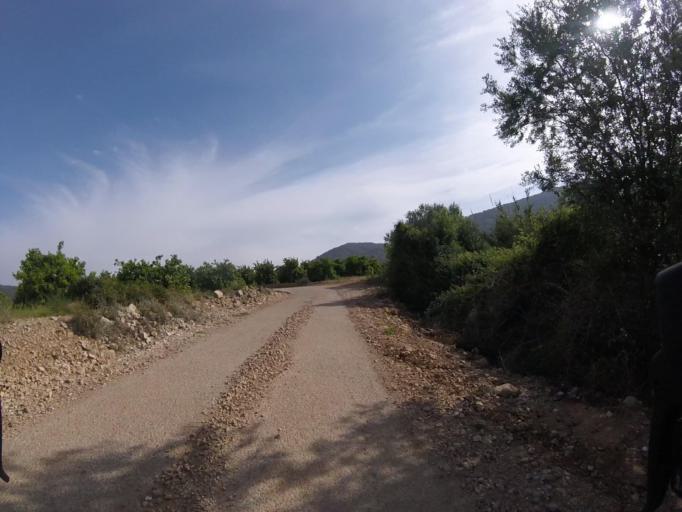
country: ES
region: Valencia
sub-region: Provincia de Castello
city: Alcala de Xivert
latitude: 40.2829
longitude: 0.2651
